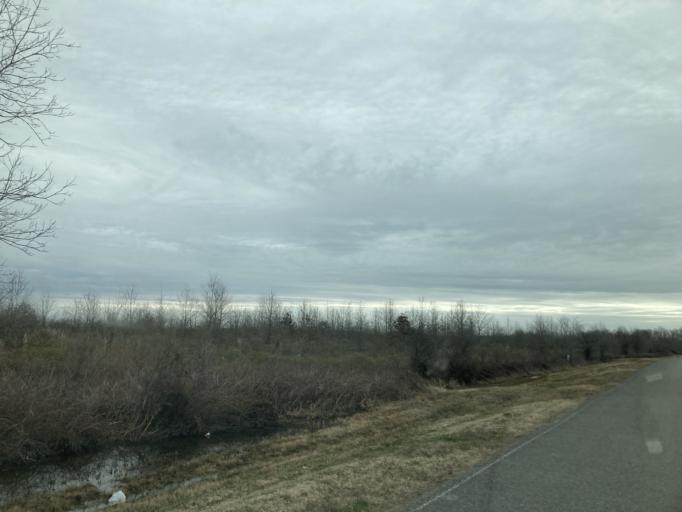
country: US
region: Mississippi
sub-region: Yazoo County
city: Yazoo City
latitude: 33.0026
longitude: -90.4683
